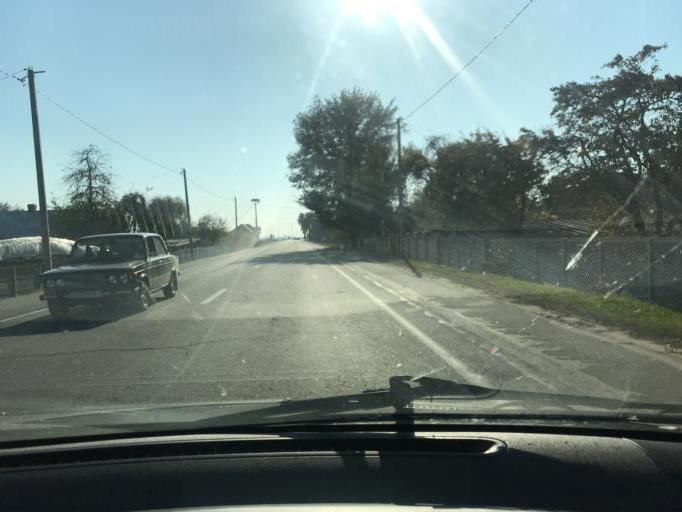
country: BY
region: Brest
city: Davyd-Haradok
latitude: 52.0714
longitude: 27.3383
